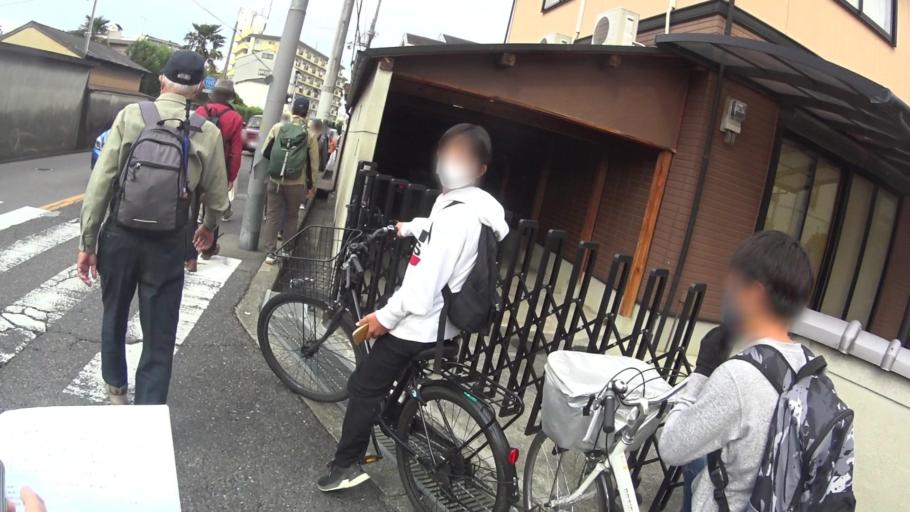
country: JP
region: Osaka
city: Kashihara
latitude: 34.5595
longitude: 135.5925
